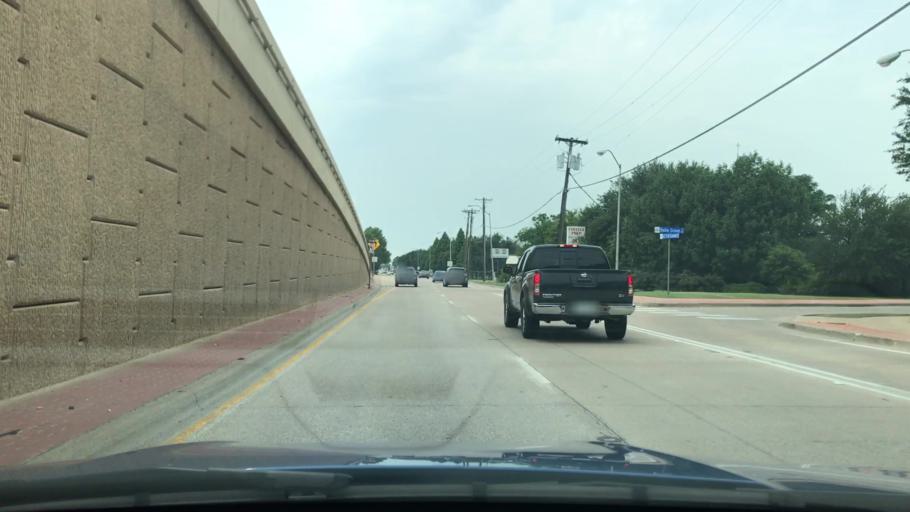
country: US
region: Texas
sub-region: Dallas County
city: Richardson
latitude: 32.9587
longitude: -96.7299
